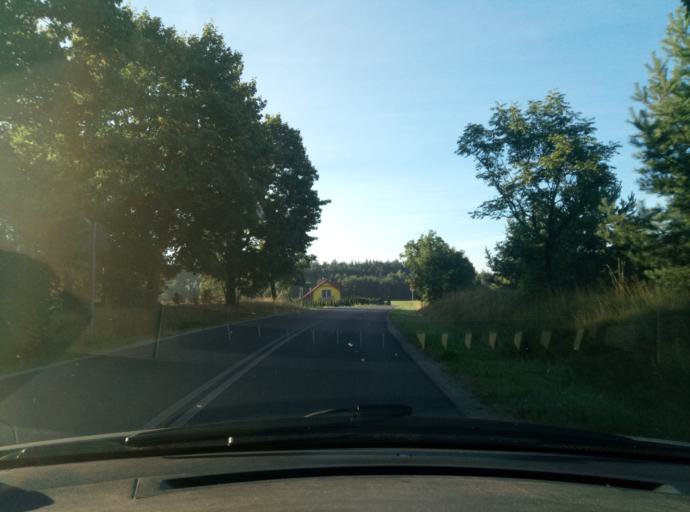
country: PL
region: Kujawsko-Pomorskie
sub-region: Powiat wabrzeski
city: Wabrzezno
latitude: 53.2333
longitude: 18.9524
